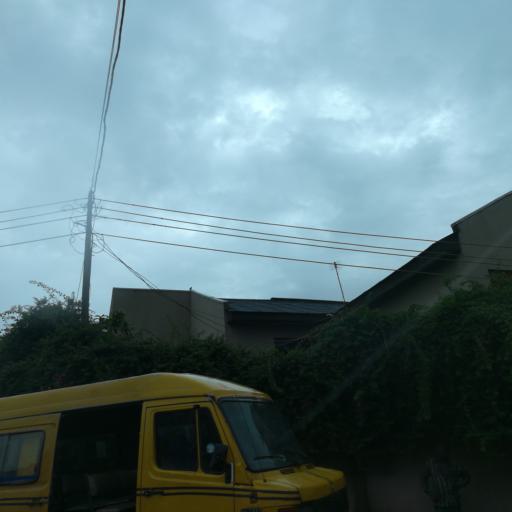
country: NG
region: Lagos
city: Oshodi
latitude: 6.5537
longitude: 3.3439
